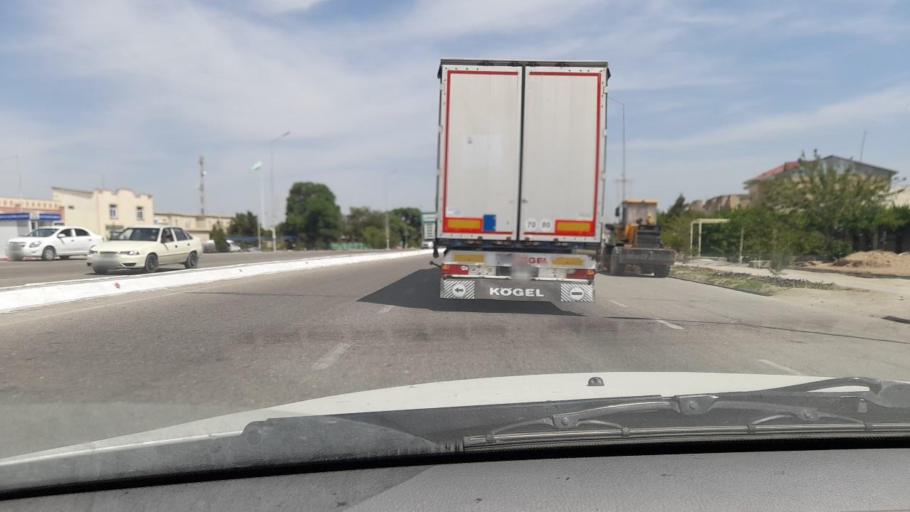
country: UZ
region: Bukhara
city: Galaosiyo
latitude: 39.8569
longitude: 64.4422
